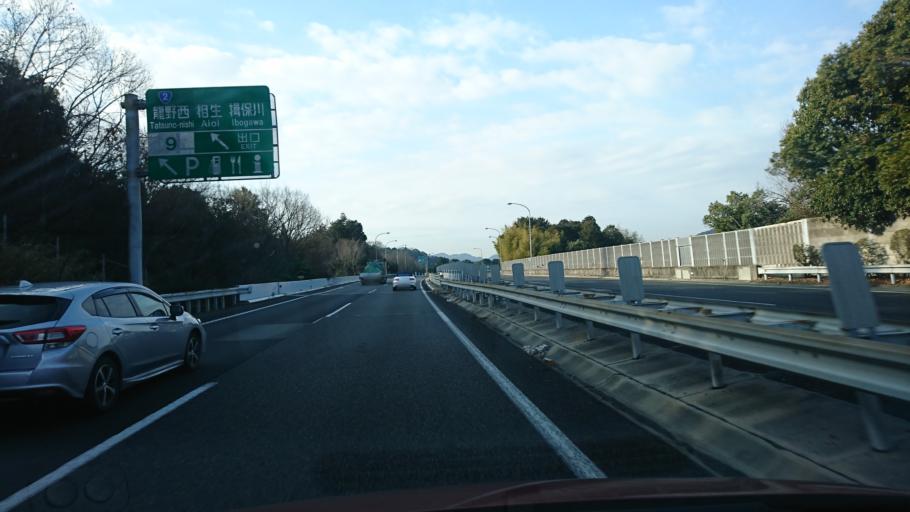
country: JP
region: Hyogo
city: Tatsunocho-tominaga
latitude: 34.8366
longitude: 134.5094
